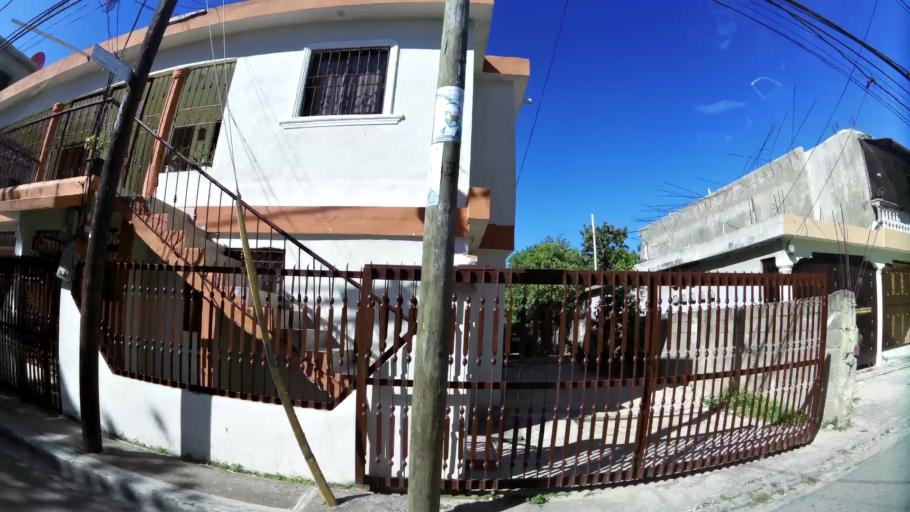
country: DO
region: San Cristobal
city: San Cristobal
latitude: 18.4312
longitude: -70.1216
